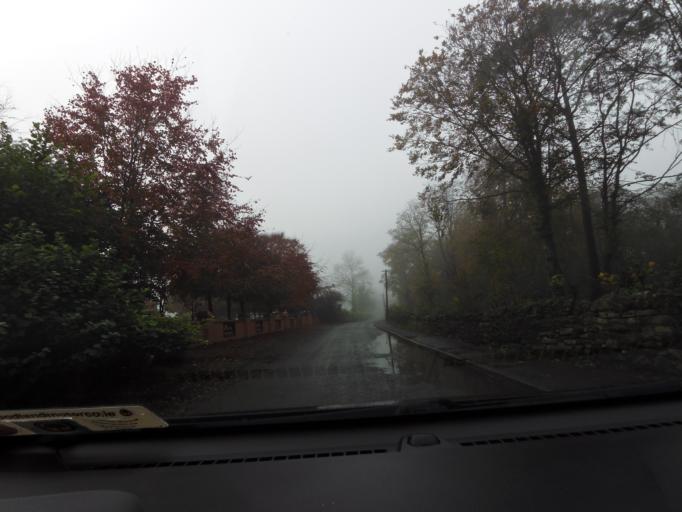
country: IE
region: Leinster
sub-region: An Iarmhi
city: Moate
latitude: 53.3749
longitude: -7.8004
